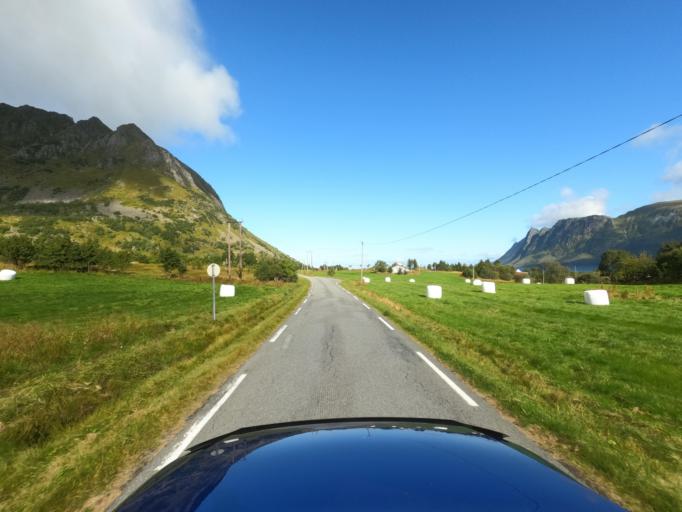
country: NO
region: Nordland
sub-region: Vagan
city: Kabelvag
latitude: 68.2901
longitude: 14.2659
